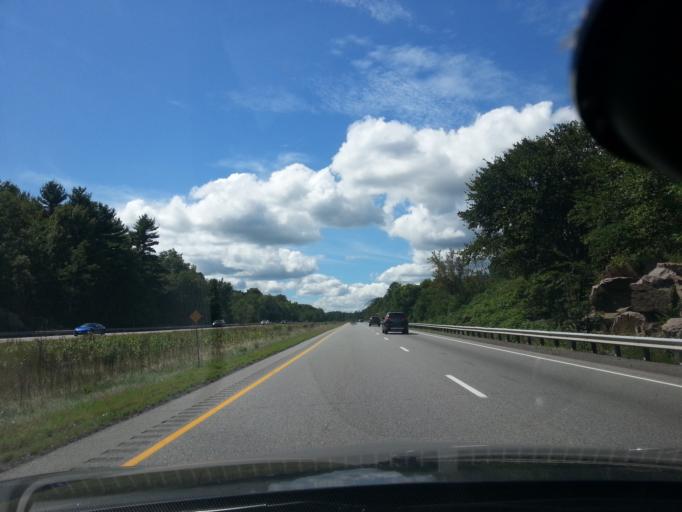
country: CA
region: Ontario
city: Brockville
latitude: 44.5186
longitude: -75.8149
